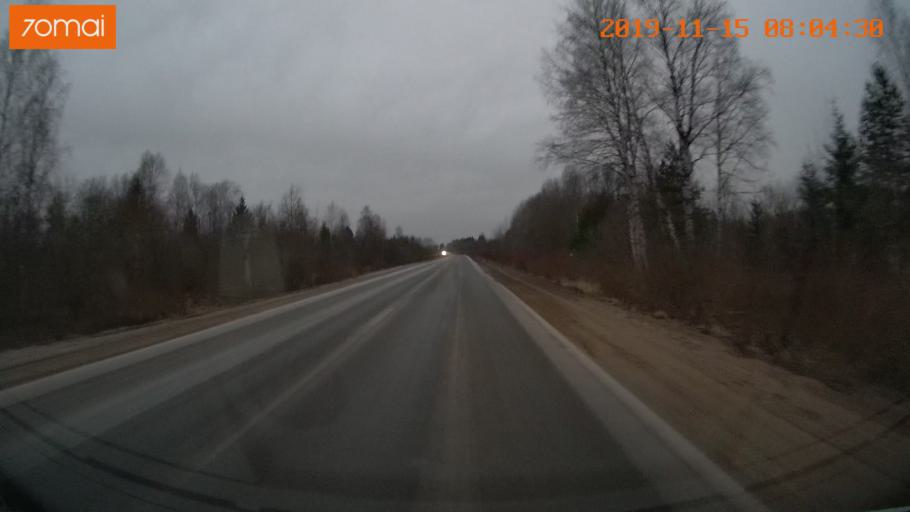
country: RU
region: Vologda
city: Cherepovets
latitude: 59.0089
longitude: 38.0749
